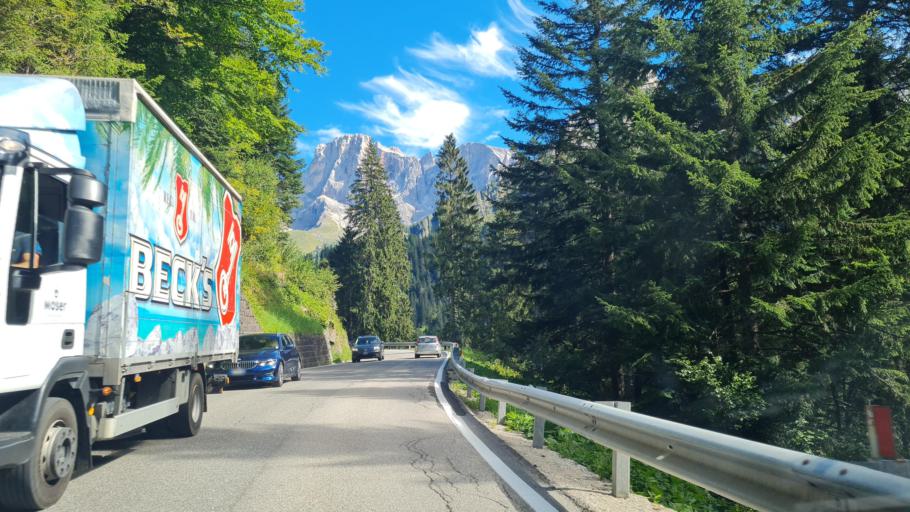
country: IT
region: Trentino-Alto Adige
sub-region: Provincia di Trento
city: Siror
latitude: 46.2399
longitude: 11.8064
